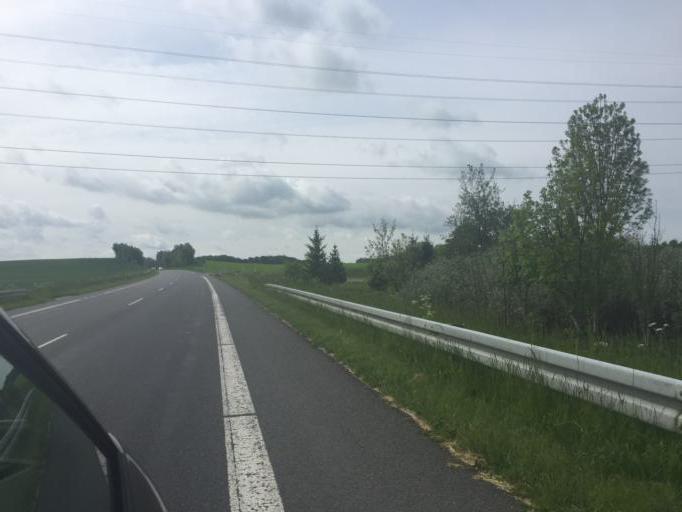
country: DK
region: Zealand
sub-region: Kalundborg Kommune
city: Hong
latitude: 55.5206
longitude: 11.3779
